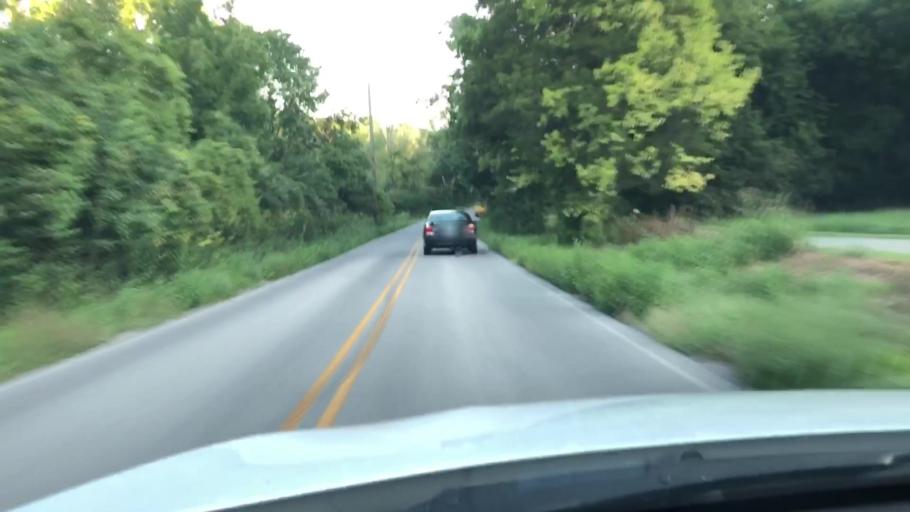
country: US
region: Kentucky
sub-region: Jefferson County
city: Middletown
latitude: 38.1942
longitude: -85.4900
